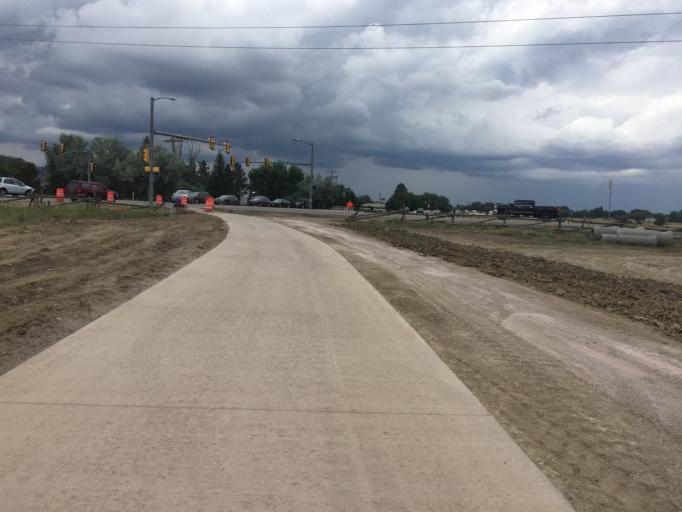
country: US
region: Colorado
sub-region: Larimer County
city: Fort Collins
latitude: 40.4939
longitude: -105.0957
